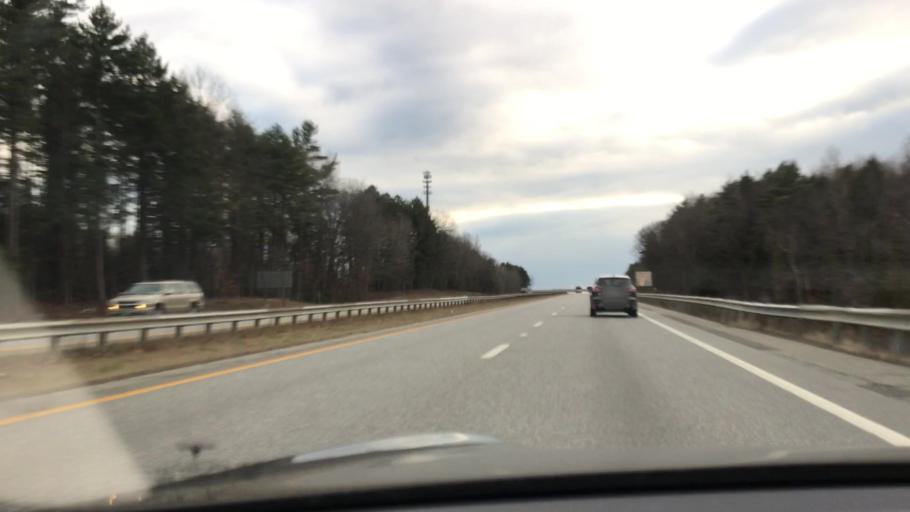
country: US
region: Maine
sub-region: Kennebec County
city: Hallowell
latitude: 44.2692
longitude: -69.8066
